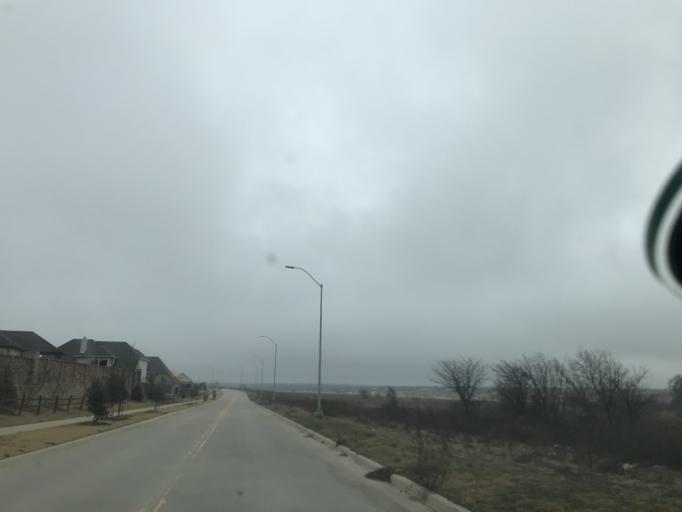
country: US
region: Texas
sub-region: Tarrant County
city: Crowley
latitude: 32.6093
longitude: -97.4187
